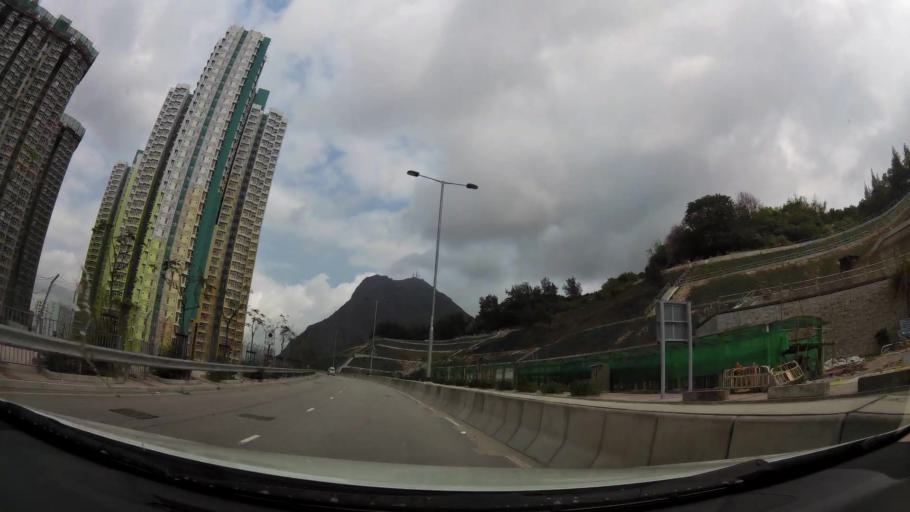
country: HK
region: Kowloon City
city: Kowloon
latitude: 22.3282
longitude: 114.2301
